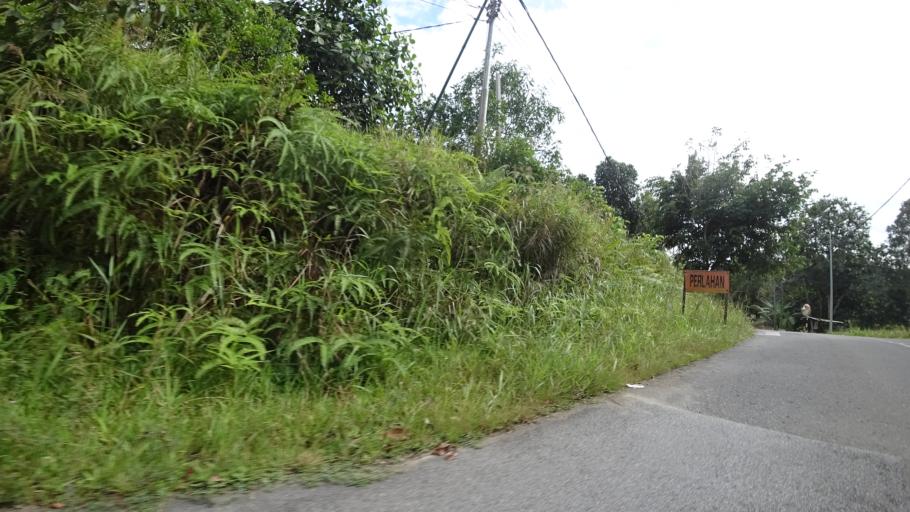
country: MY
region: Sarawak
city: Limbang
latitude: 4.8362
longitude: 114.9494
